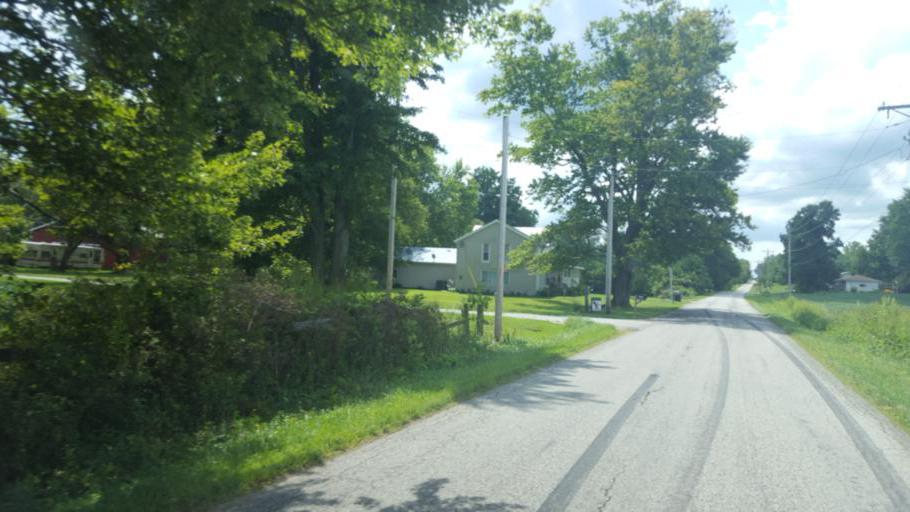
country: US
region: Ohio
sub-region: Morrow County
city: Mount Gilead
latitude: 40.4838
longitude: -82.7535
